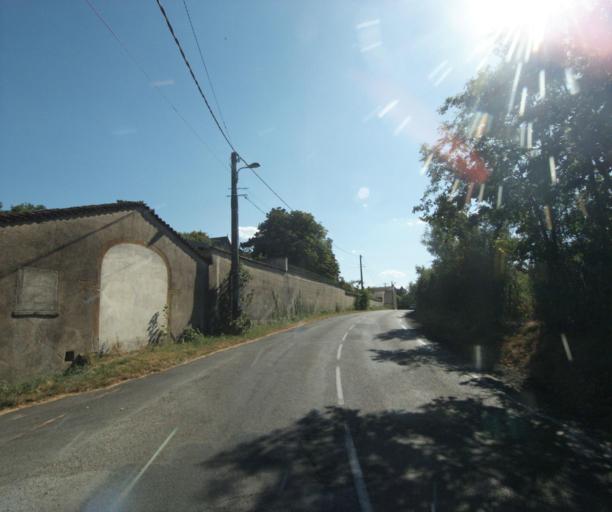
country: FR
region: Rhone-Alpes
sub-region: Departement du Rhone
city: La Tour-de-Salvagny
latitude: 45.8402
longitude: 4.7231
